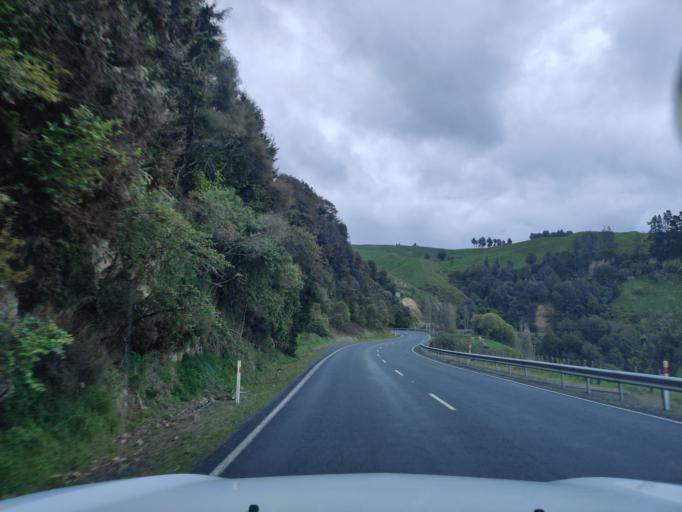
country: NZ
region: Waikato
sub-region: Otorohanga District
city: Otorohanga
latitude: -38.4991
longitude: 175.1948
